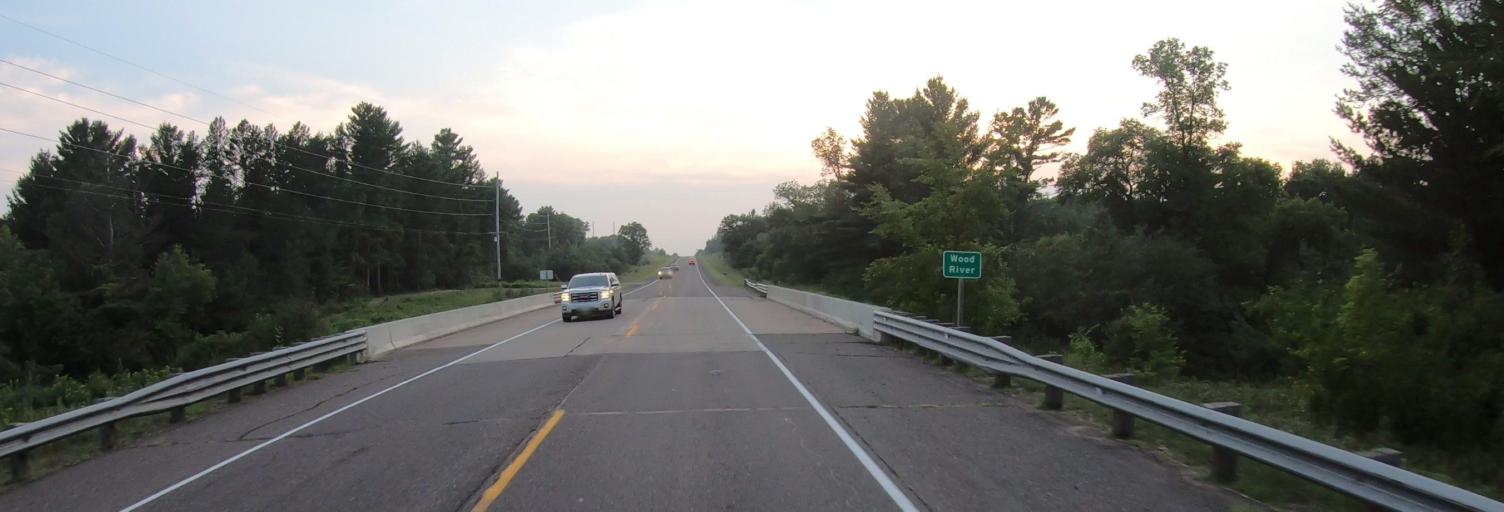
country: US
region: Wisconsin
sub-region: Burnett County
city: Grantsburg
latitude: 45.7731
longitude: -92.7074
